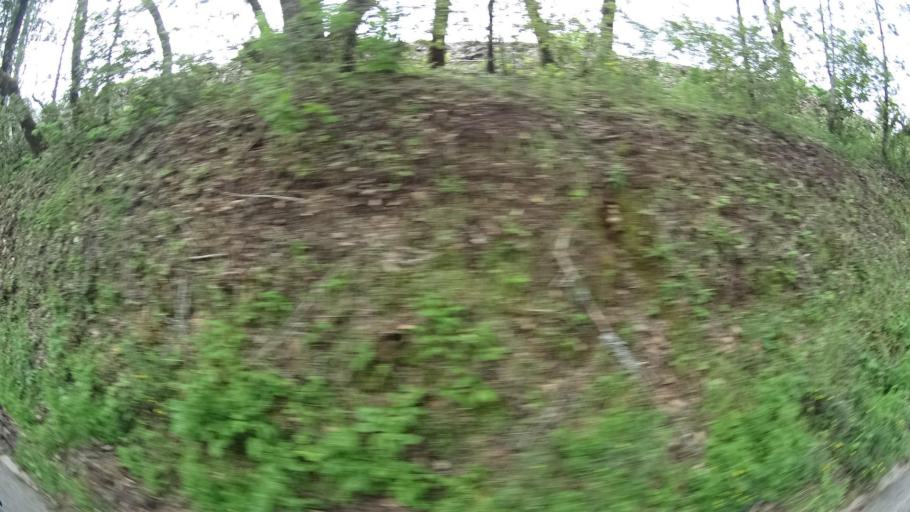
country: US
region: California
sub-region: Humboldt County
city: Redway
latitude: 40.0929
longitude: -123.8027
